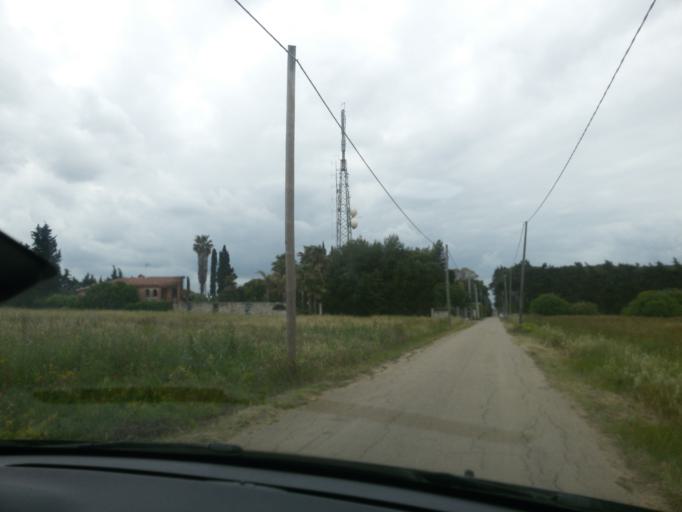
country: IT
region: Apulia
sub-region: Provincia di Brindisi
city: Brindisi
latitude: 40.6387
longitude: 17.8960
